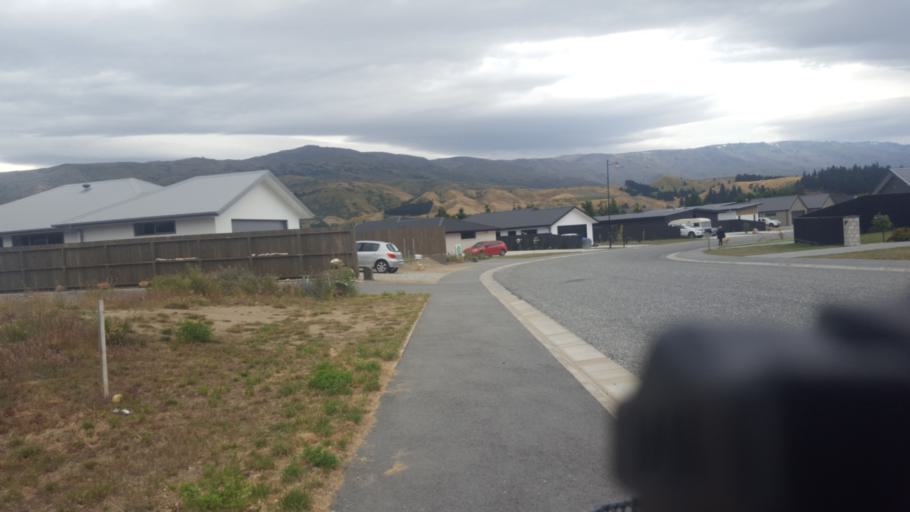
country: NZ
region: Otago
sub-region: Queenstown-Lakes District
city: Wanaka
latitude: -45.0481
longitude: 169.1823
